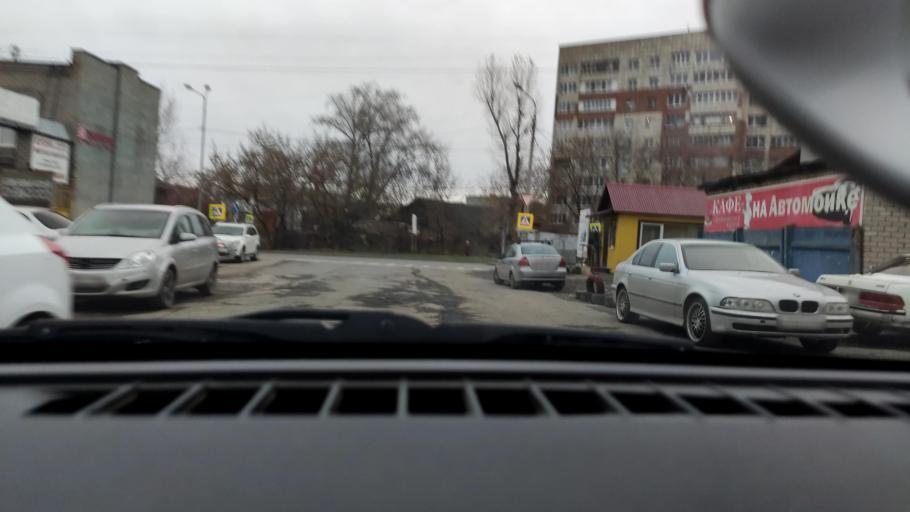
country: RU
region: Perm
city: Kondratovo
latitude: 57.9606
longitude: 56.1639
